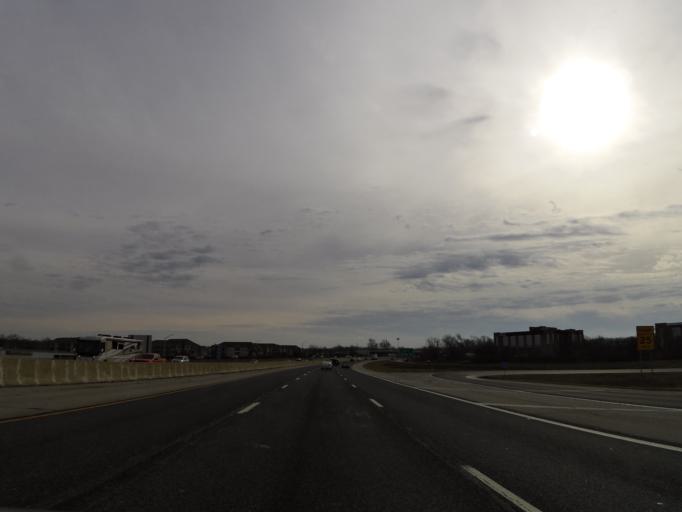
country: US
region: Indiana
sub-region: Marion County
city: Lawrence
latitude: 39.8947
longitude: -86.0539
